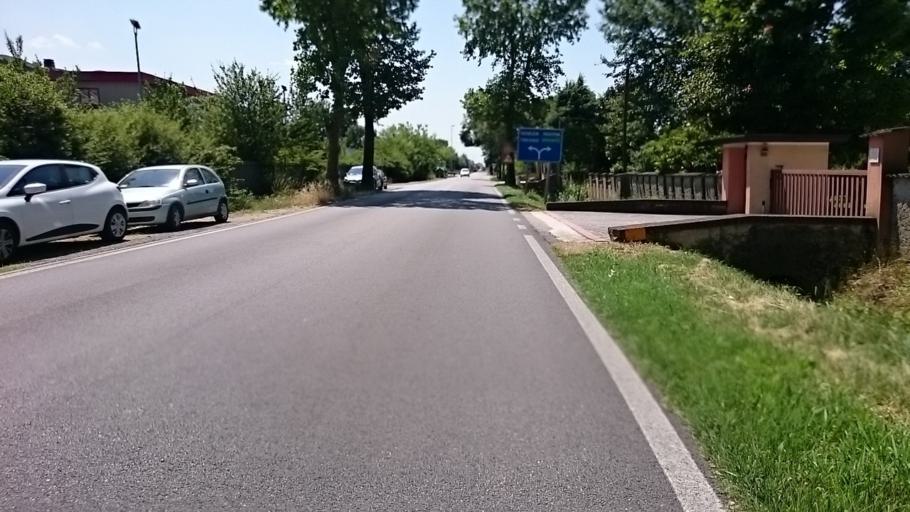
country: IT
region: Veneto
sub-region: Provincia di Venezia
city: Sant'Angelo
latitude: 45.5101
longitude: 12.0132
